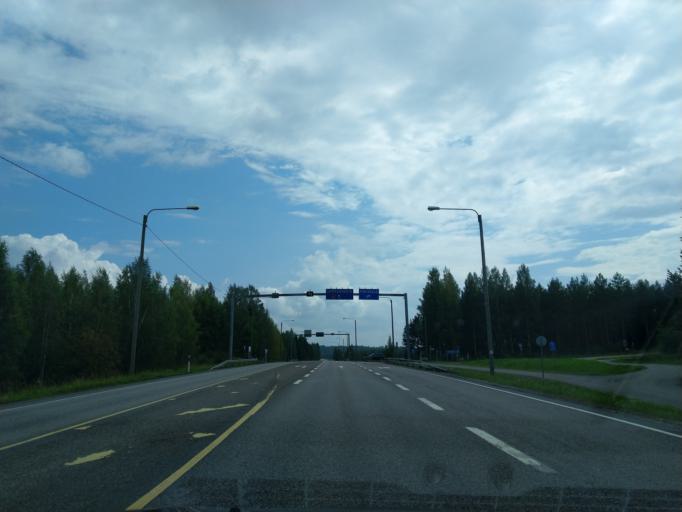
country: FI
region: South Karelia
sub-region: Imatra
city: Parikkala
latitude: 61.5874
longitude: 29.4925
